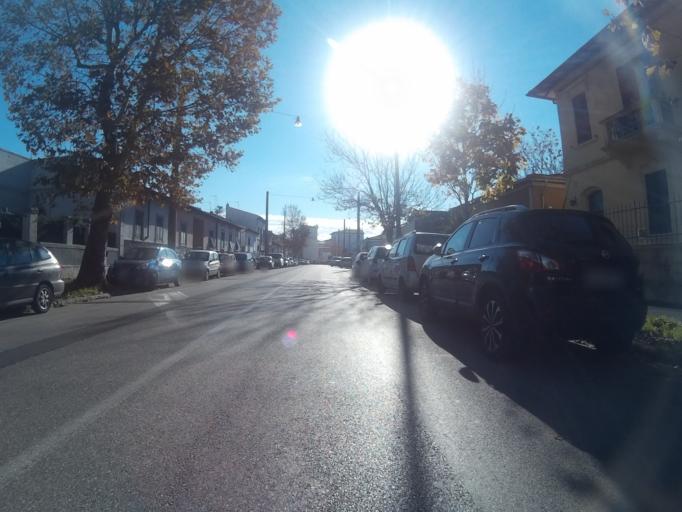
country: IT
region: Tuscany
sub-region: Provincia di Livorno
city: Livorno
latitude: 43.5630
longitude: 10.3186
